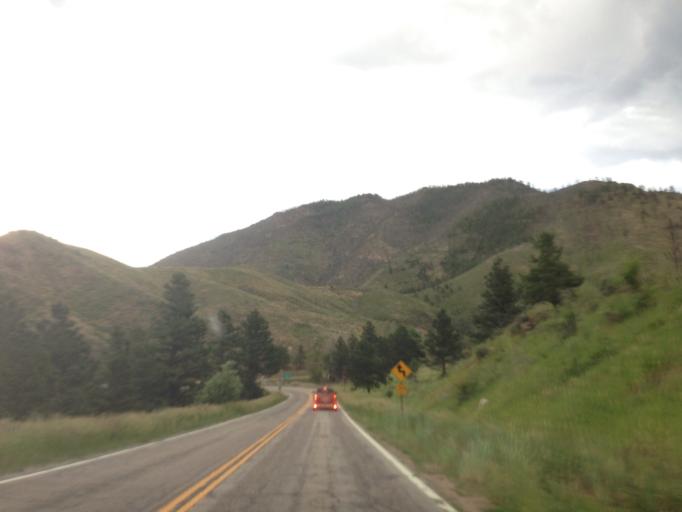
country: US
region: Colorado
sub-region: Larimer County
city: Laporte
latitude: 40.6825
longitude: -105.3919
